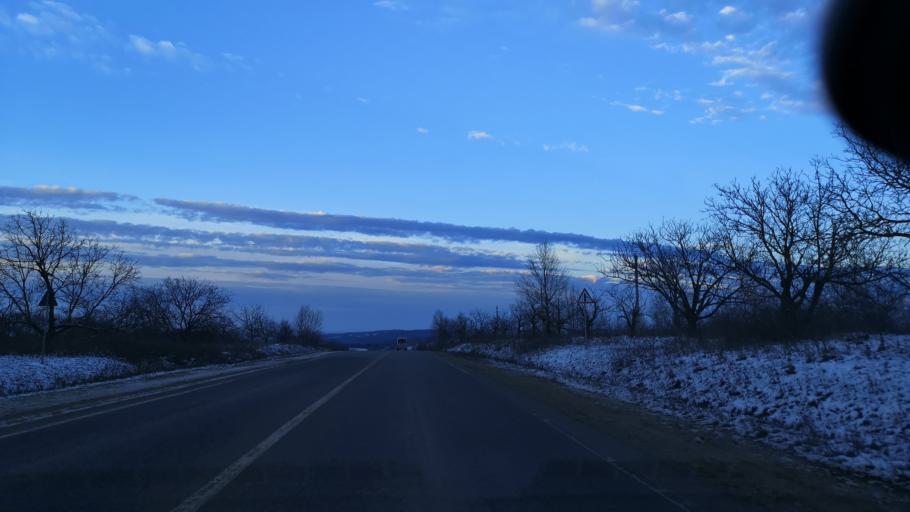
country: MD
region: Orhei
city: Orhei
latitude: 47.5354
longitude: 28.7933
